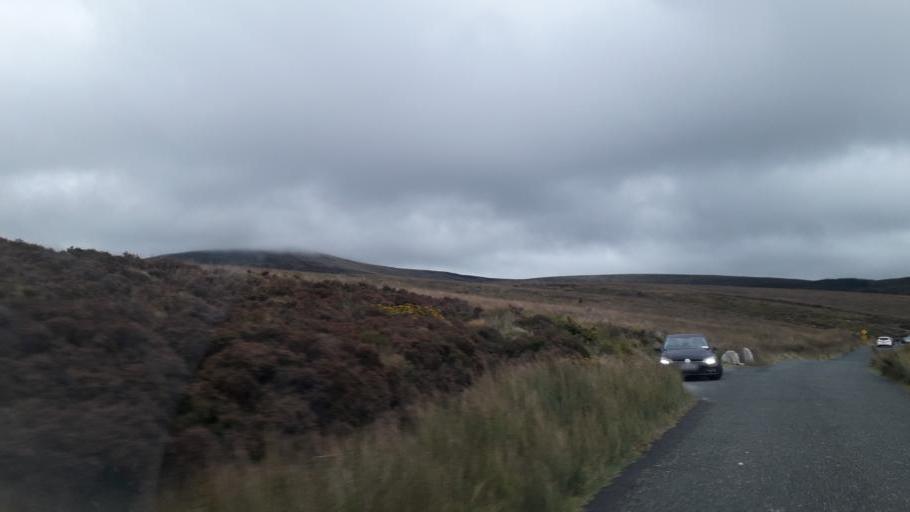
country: IE
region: Leinster
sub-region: Wicklow
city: Enniskerry
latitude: 53.1250
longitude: -6.2810
